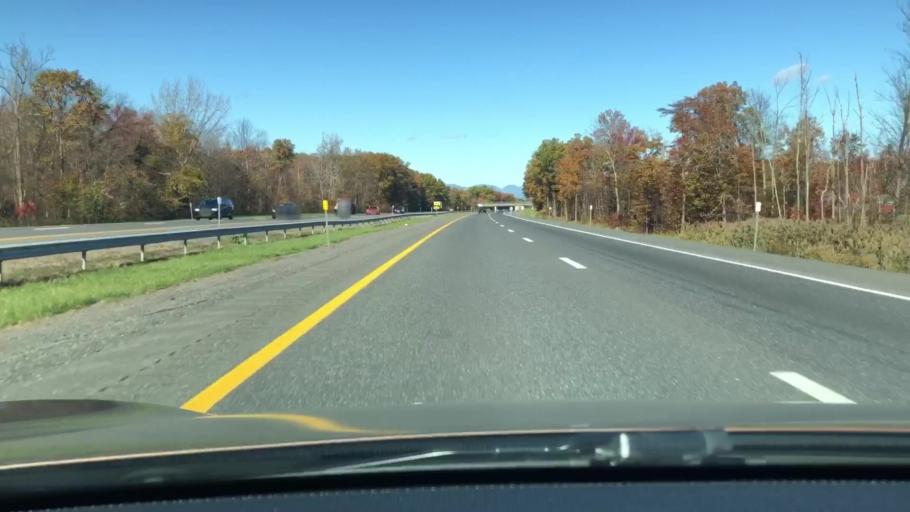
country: US
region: New York
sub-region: Ulster County
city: Plattekill
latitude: 41.6545
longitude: -74.0778
